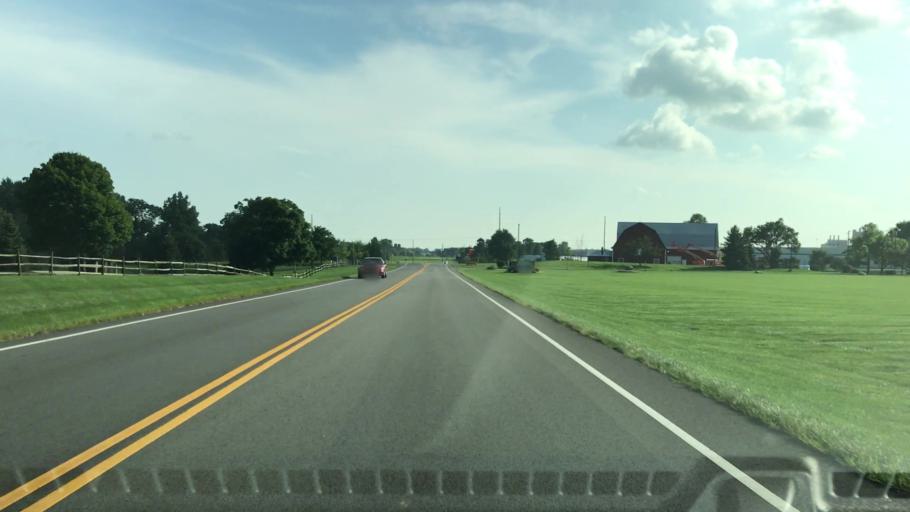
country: US
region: Ohio
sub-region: Union County
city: Marysville
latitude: 40.2096
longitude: -83.3115
